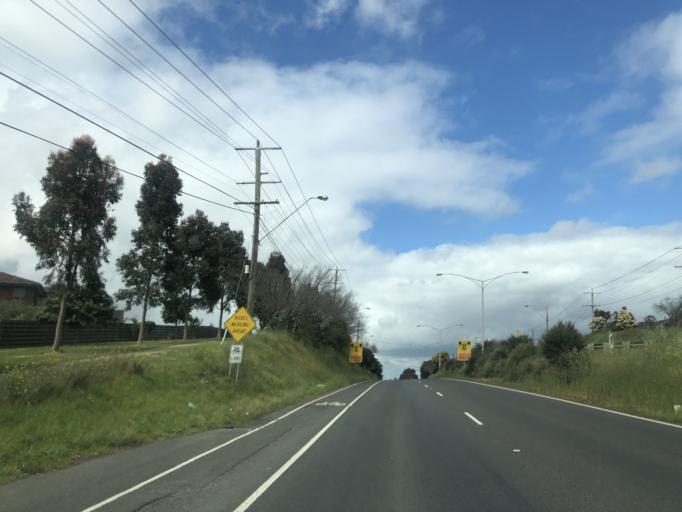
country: AU
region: Victoria
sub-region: Knox
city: Rowville
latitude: -37.9531
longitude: 145.2268
